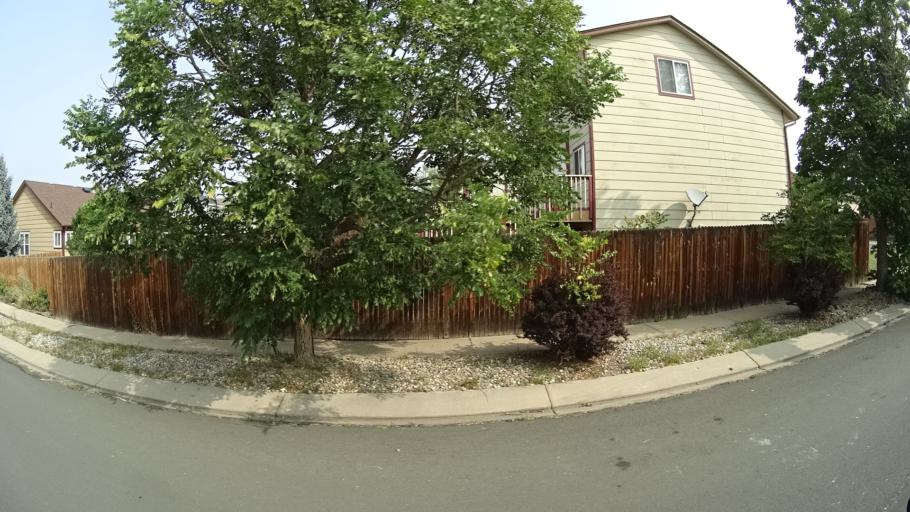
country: US
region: Colorado
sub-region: El Paso County
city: Cimarron Hills
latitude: 38.9270
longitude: -104.7355
